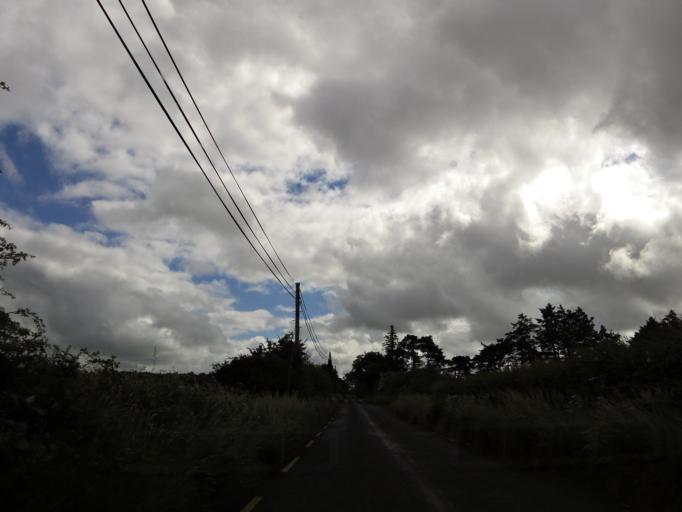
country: IE
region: Connaught
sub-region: County Galway
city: Loughrea
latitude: 53.4249
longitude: -8.5034
